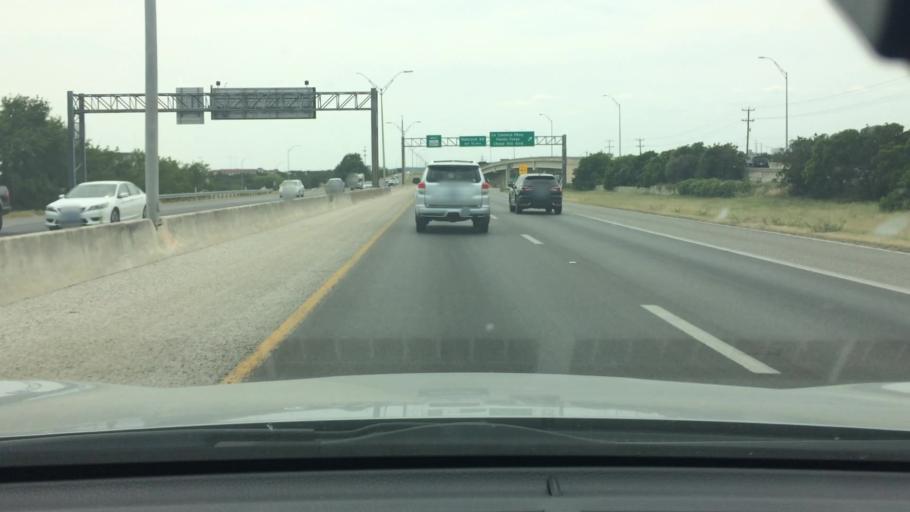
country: US
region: Texas
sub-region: Bexar County
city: Shavano Park
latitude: 29.5893
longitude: -98.6129
